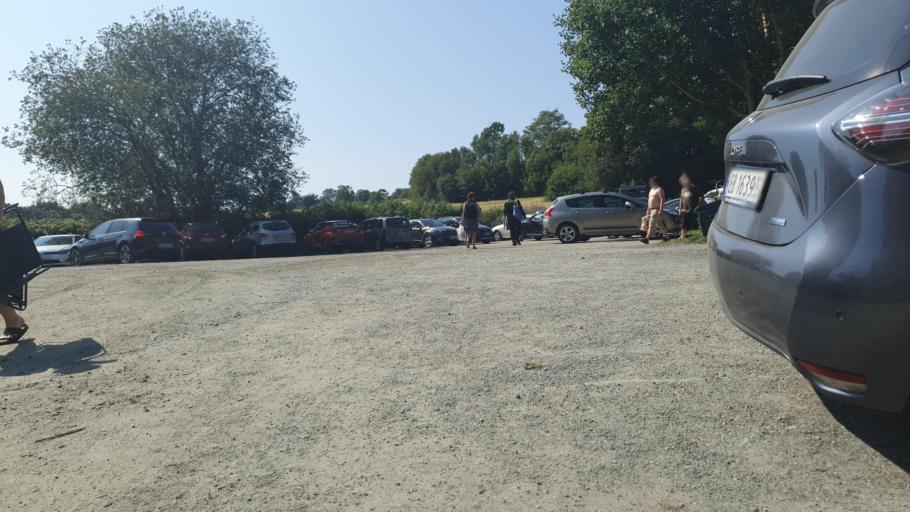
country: NO
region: Sor-Trondelag
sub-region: Trondheim
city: Trondheim
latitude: 63.4526
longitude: 10.4603
